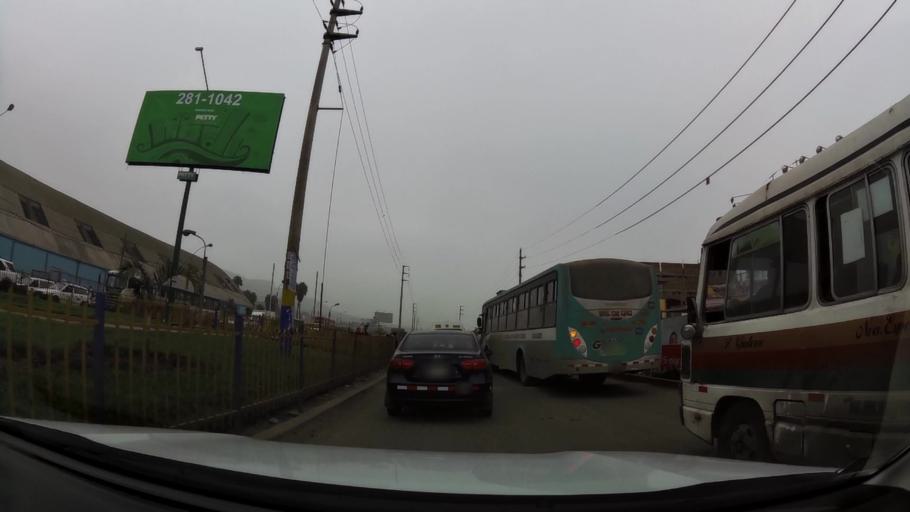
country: PE
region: Lima
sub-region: Lima
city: Surco
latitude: -12.1733
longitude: -76.9480
